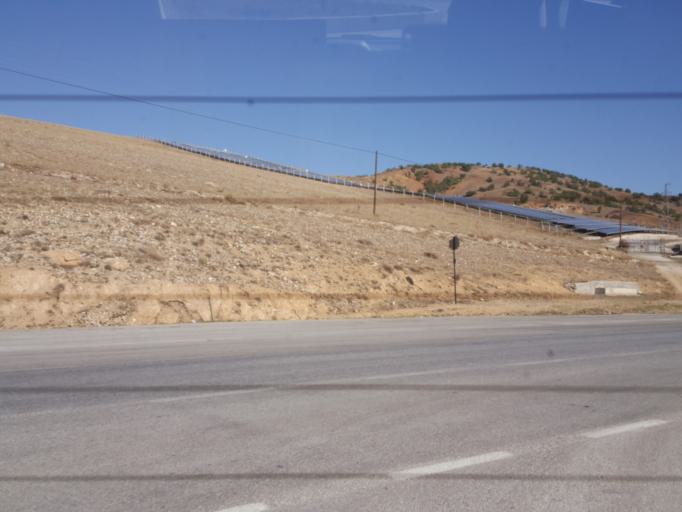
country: TR
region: Corum
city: Sungurlu
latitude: 40.2199
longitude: 34.5600
